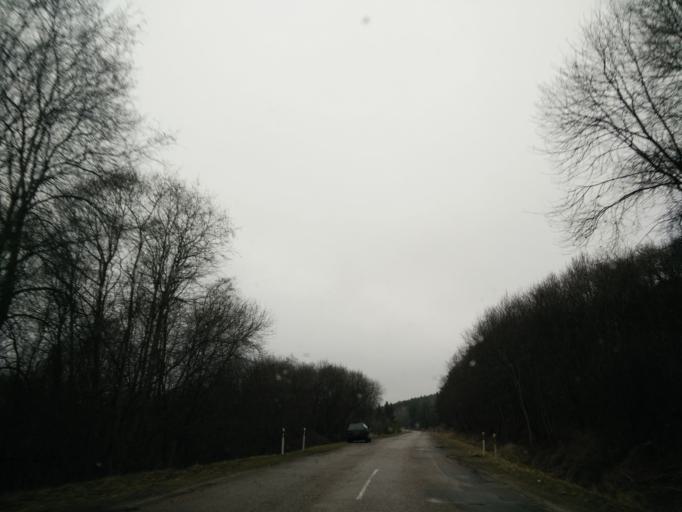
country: LT
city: Ariogala
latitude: 55.2898
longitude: 23.4433
